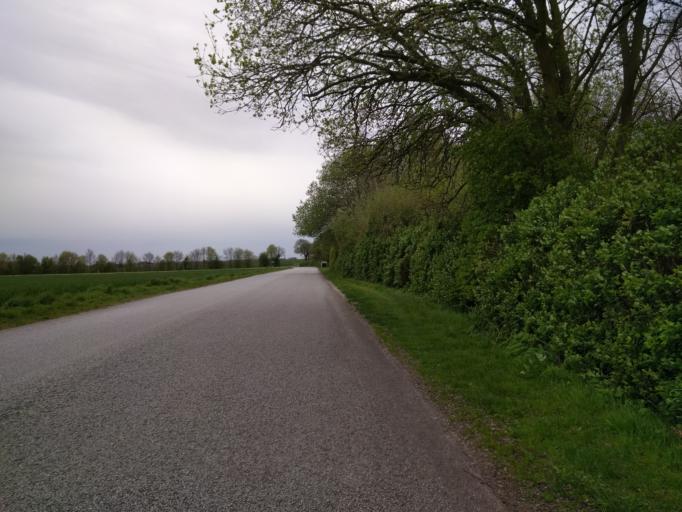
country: DK
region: South Denmark
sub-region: Kerteminde Kommune
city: Munkebo
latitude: 55.4666
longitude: 10.5915
